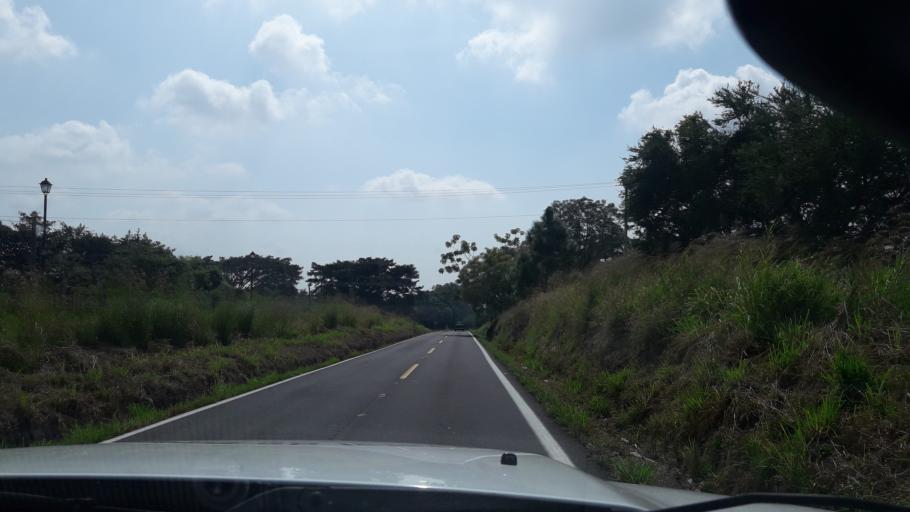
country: MX
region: Colima
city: Suchitlan
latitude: 19.3832
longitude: -103.7117
